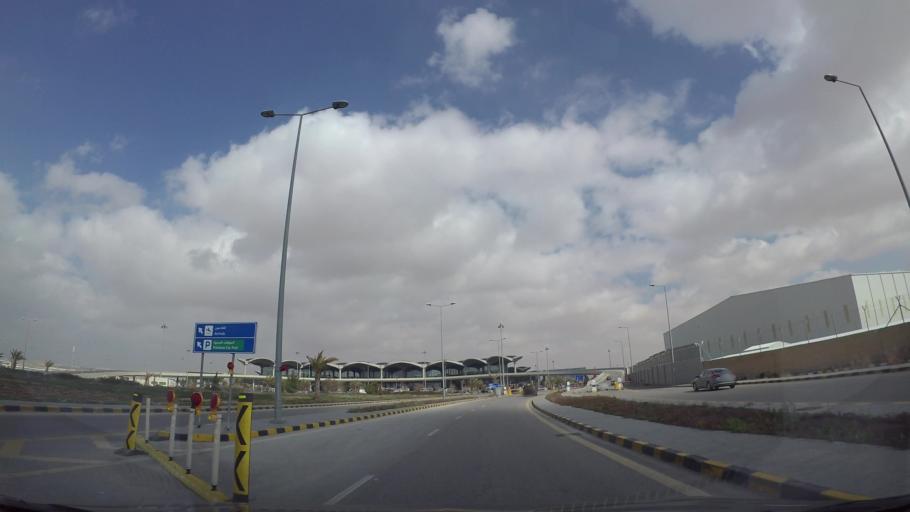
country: JO
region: Amman
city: Al Jizah
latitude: 31.7212
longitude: 35.9820
